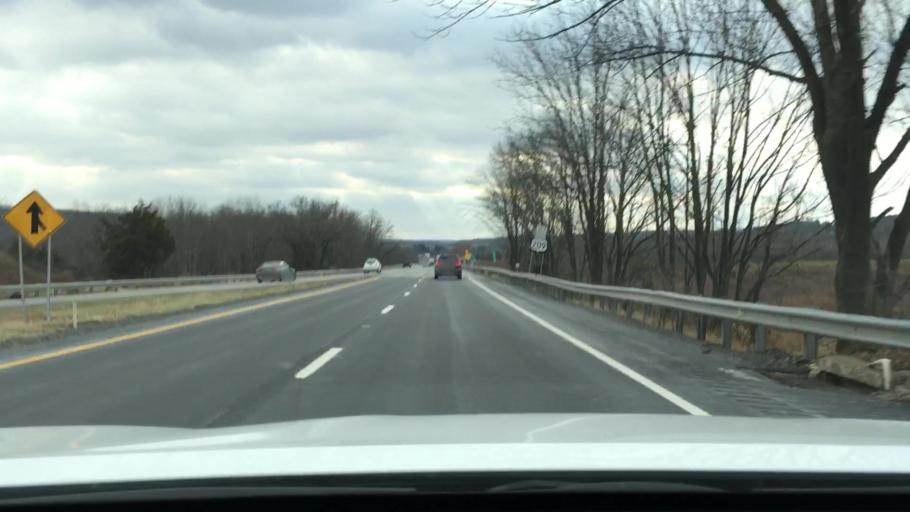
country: US
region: Pennsylvania
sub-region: Monroe County
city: Saylorsburg
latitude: 40.9587
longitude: -75.2854
